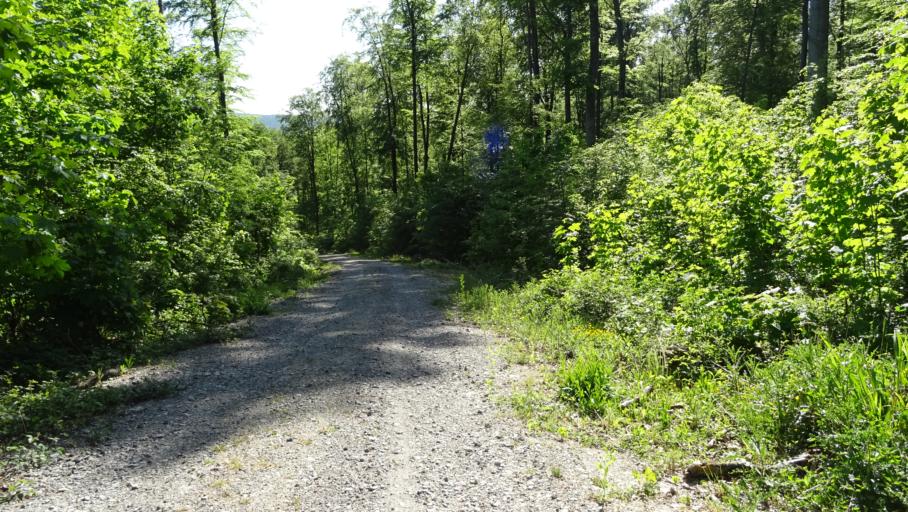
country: DE
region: Baden-Wuerttemberg
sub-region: Karlsruhe Region
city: Obrigheim
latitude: 49.3718
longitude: 9.1106
